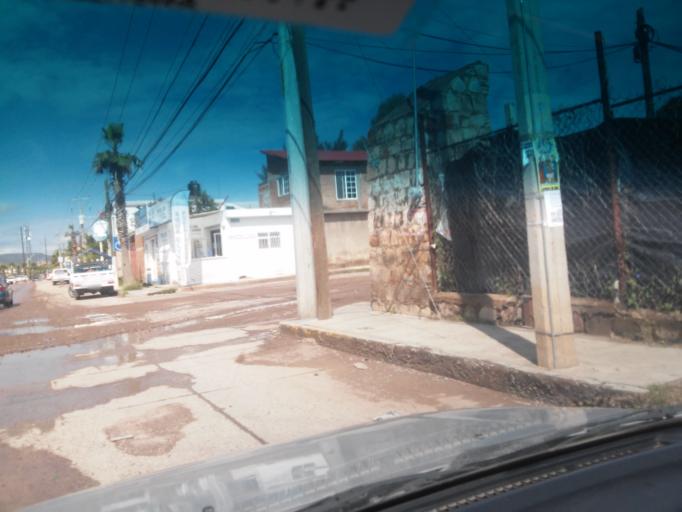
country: MX
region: Durango
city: Victoria de Durango
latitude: 24.0094
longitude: -104.6968
